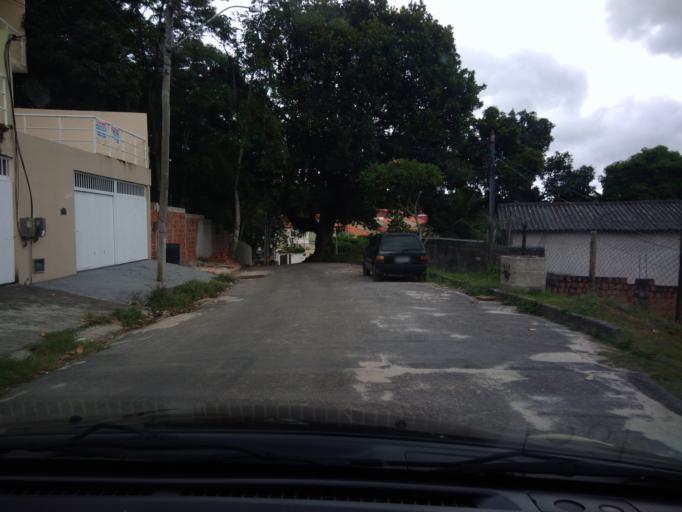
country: BR
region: Rio de Janeiro
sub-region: Niteroi
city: Niteroi
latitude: -22.9320
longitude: -43.0122
